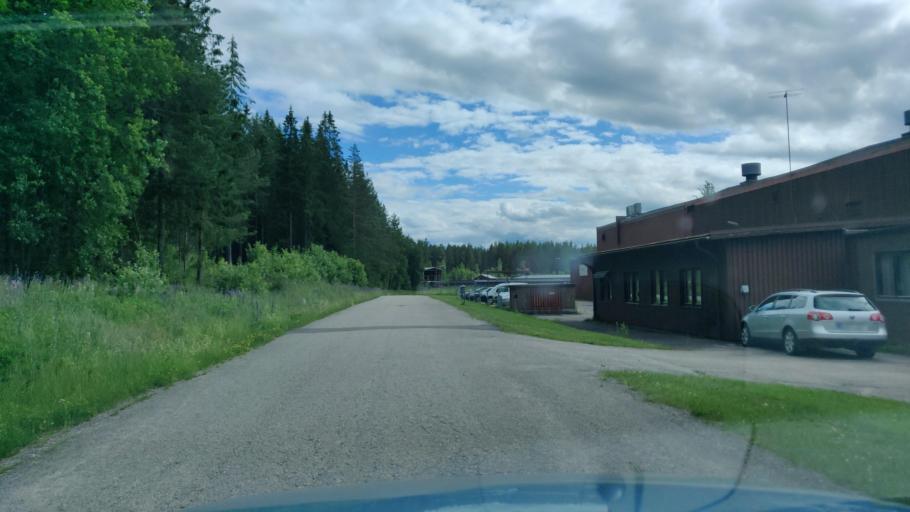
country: SE
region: Vaermland
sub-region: Hagfors Kommun
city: Hagfors
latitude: 60.0464
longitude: 13.7122
